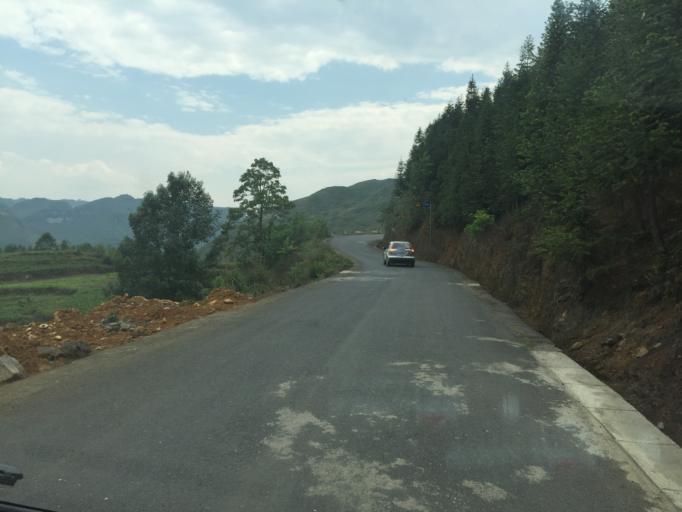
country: CN
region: Guangxi Zhuangzu Zizhiqu
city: Xinzhou
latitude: 25.6575
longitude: 105.2346
